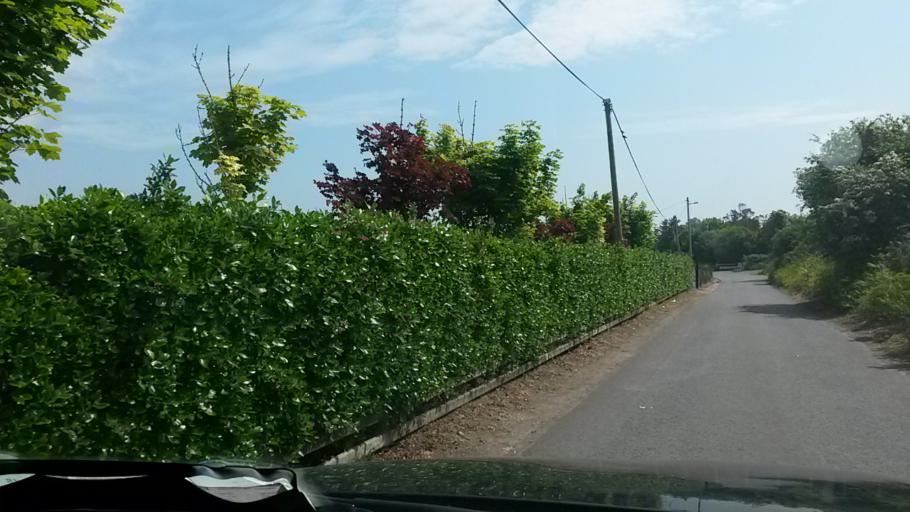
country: IE
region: Leinster
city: Portraine
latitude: 53.5040
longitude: -6.1229
